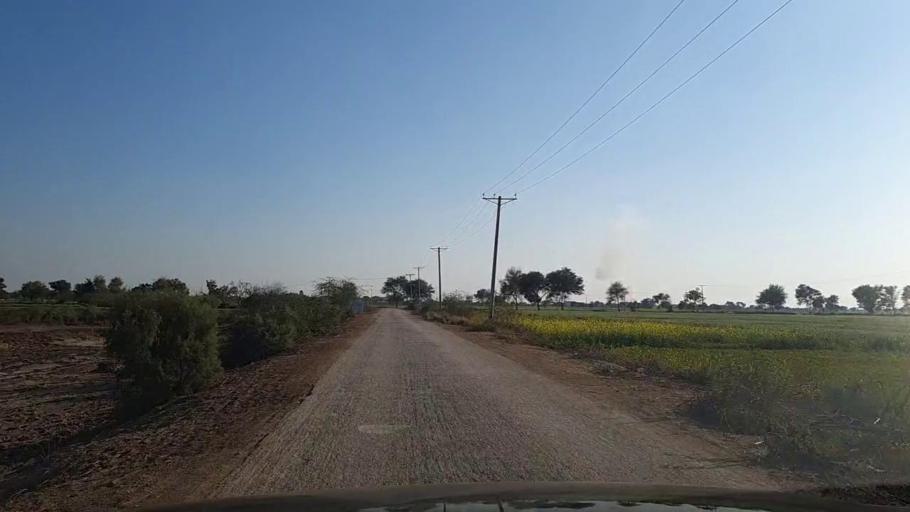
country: PK
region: Sindh
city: Nawabshah
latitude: 26.2108
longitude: 68.3739
